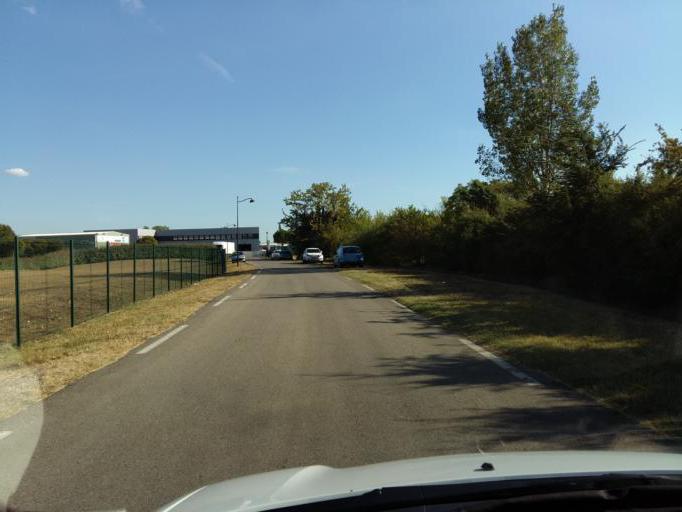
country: FR
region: Provence-Alpes-Cote d'Azur
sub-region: Departement du Vaucluse
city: Le Thor
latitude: 43.9244
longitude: 5.0166
